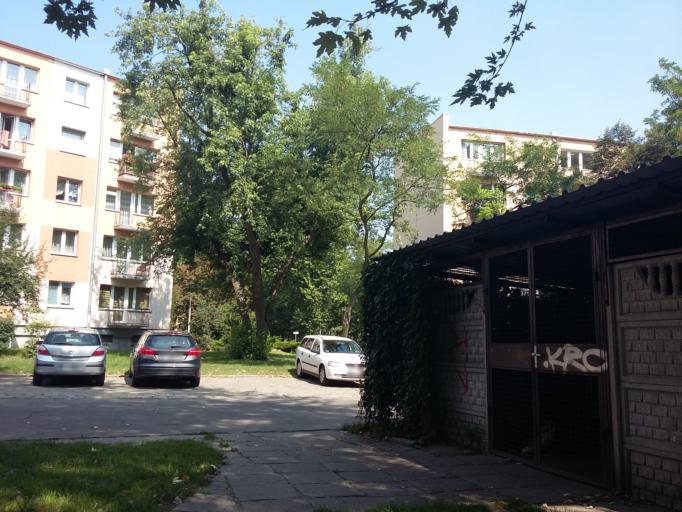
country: PL
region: Lodz Voivodeship
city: Lodz
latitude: 51.7440
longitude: 19.4148
